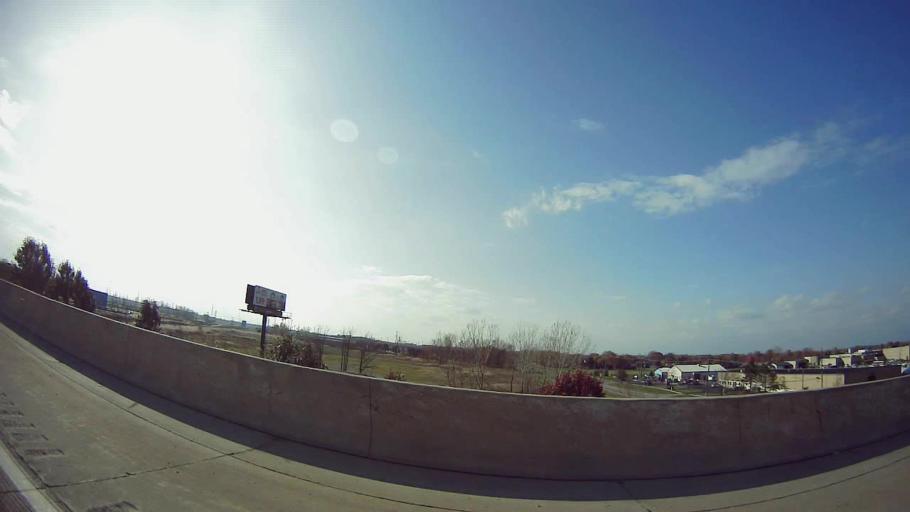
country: US
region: Michigan
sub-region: Wayne County
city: Woodhaven
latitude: 42.1239
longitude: -83.2415
